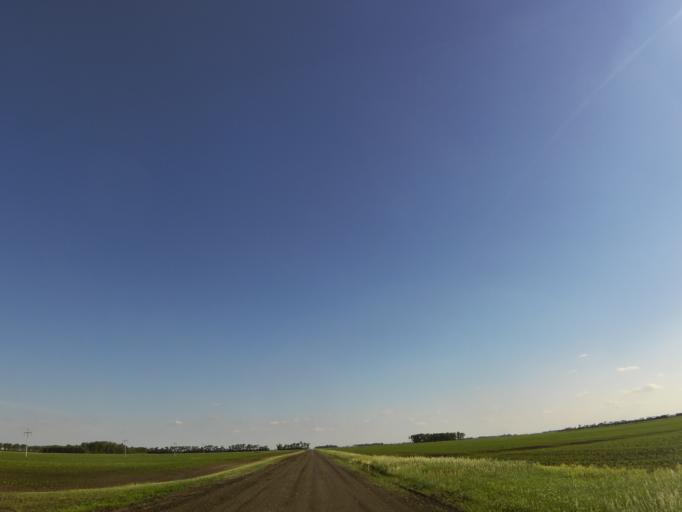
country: US
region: North Dakota
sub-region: Walsh County
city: Grafton
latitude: 48.4050
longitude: -97.2338
